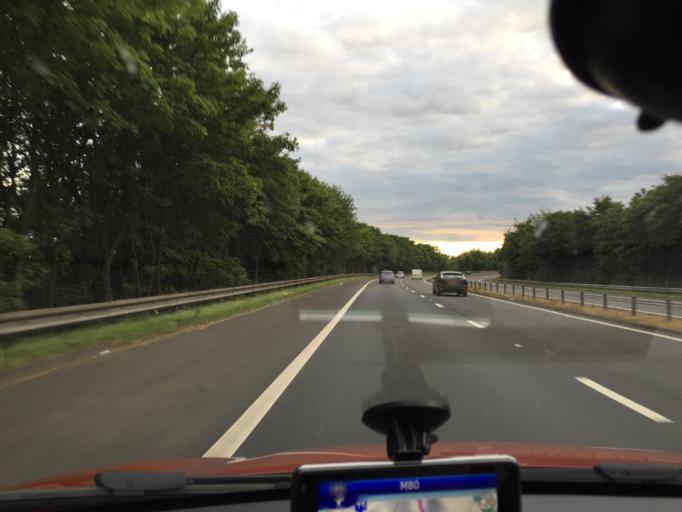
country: GB
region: Scotland
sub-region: Falkirk
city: Bonnybridge
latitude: 56.0031
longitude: -3.9040
